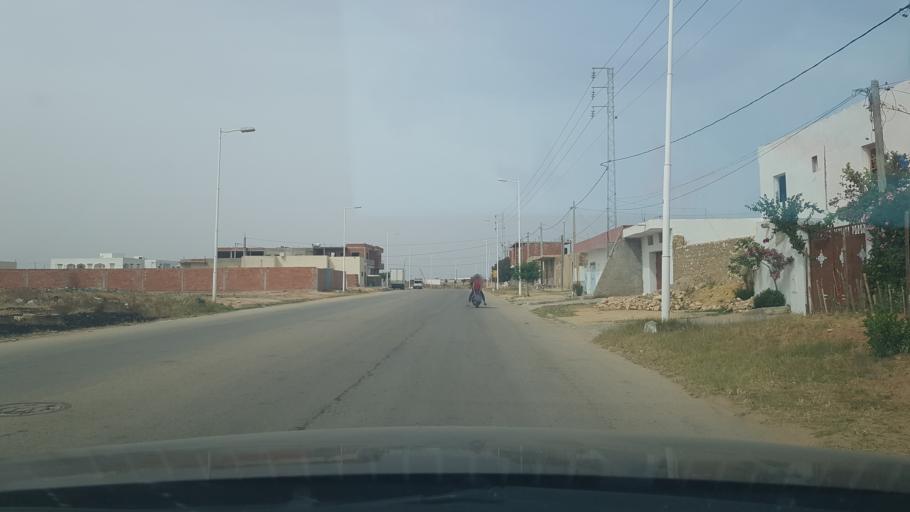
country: TN
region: Safaqis
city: Al Qarmadah
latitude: 34.8349
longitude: 10.7463
